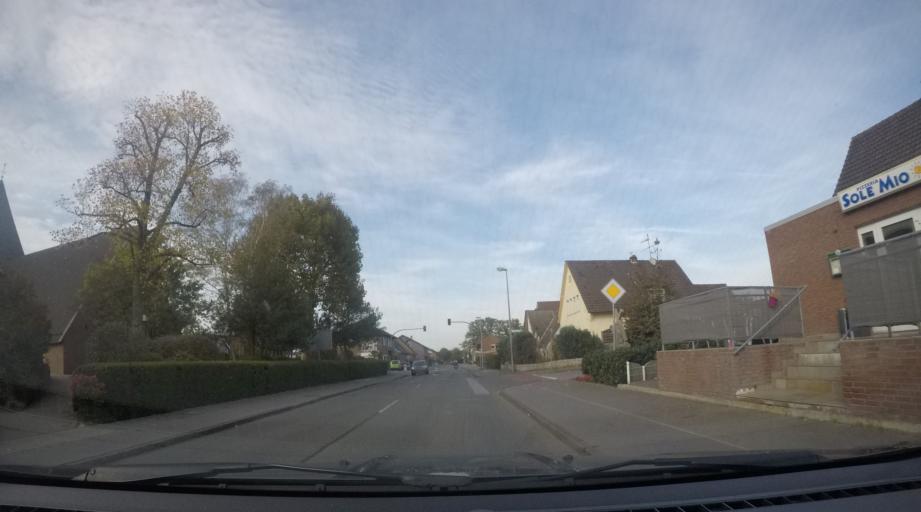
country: DE
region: North Rhine-Westphalia
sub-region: Regierungsbezirk Munster
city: Rhede
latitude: 51.8212
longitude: 6.6965
